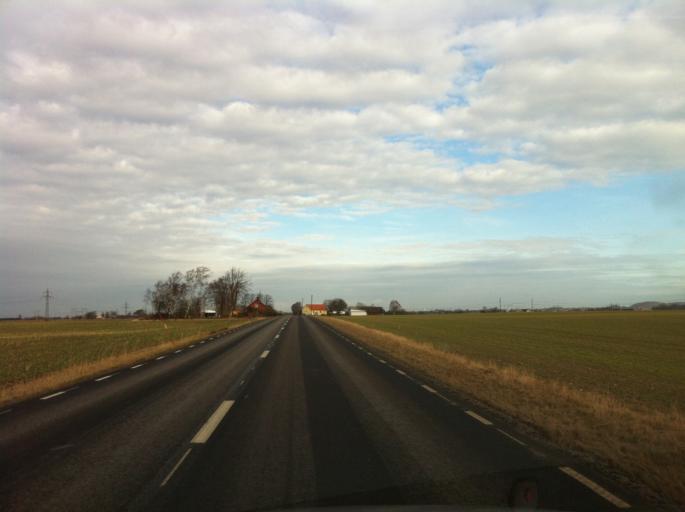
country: SE
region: Skane
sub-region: Bjuvs Kommun
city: Bjuv
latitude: 56.0913
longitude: 12.8896
